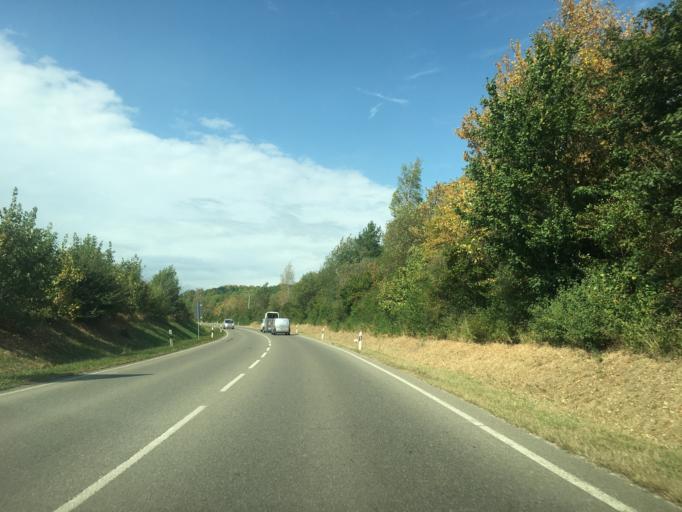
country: DE
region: Baden-Wuerttemberg
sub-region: Tuebingen Region
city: Gomaringen
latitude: 48.4489
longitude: 9.1542
